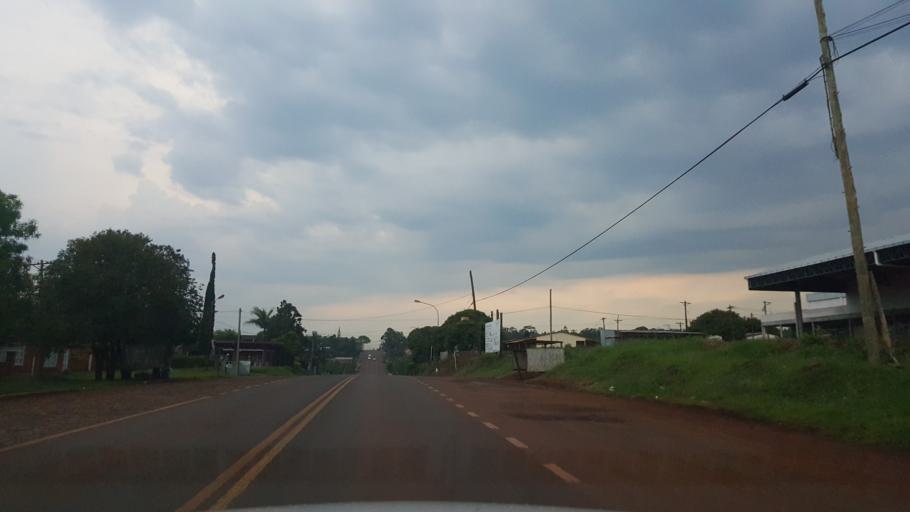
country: AR
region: Misiones
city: Gobernador Roca
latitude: -27.1960
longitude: -55.4751
